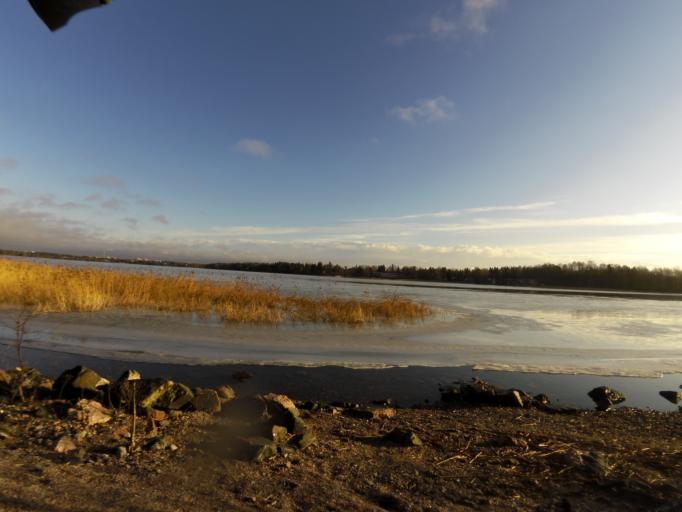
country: FI
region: Uusimaa
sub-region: Helsinki
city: Teekkarikylae
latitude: 60.1837
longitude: 24.8379
